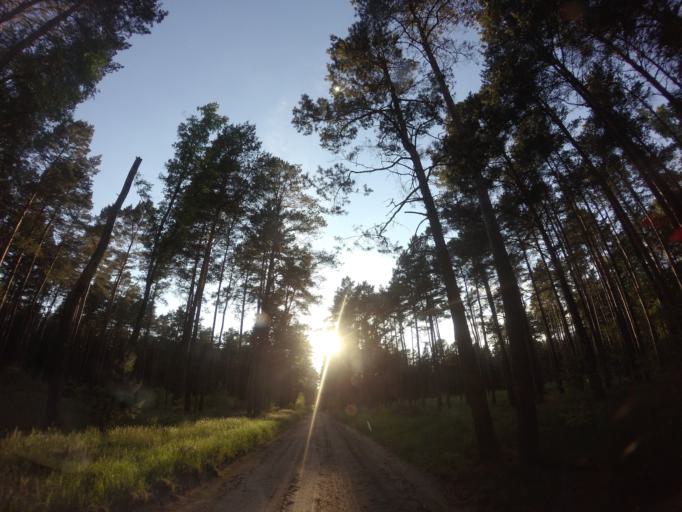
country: PL
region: West Pomeranian Voivodeship
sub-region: Powiat choszczenski
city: Drawno
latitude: 53.1405
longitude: 15.7153
